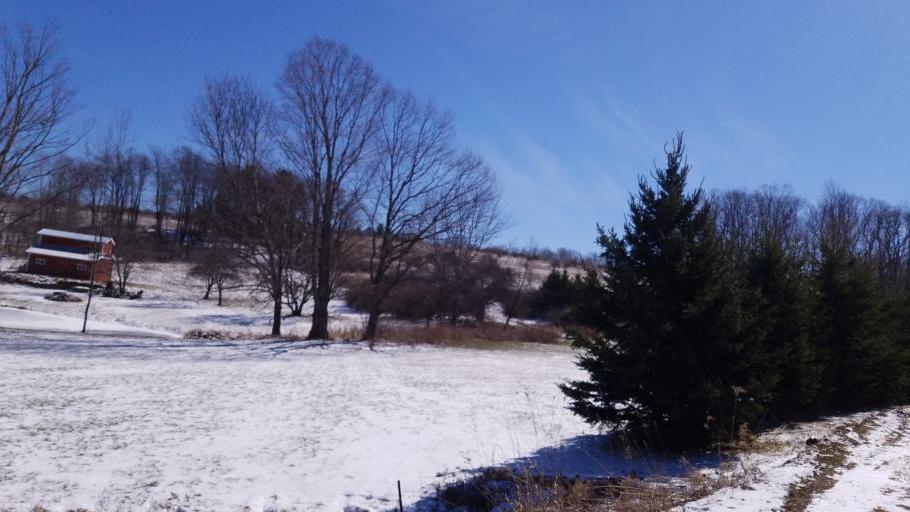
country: US
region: New York
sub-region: Allegany County
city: Andover
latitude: 42.0265
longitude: -77.7599
